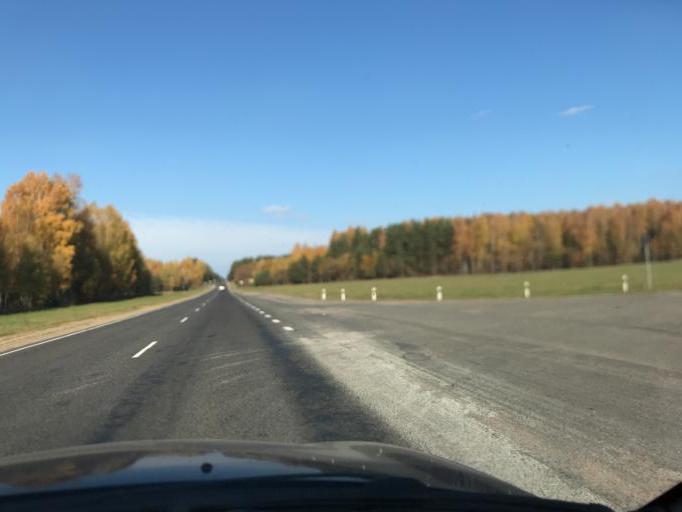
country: BY
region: Grodnenskaya
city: Lida
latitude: 53.9543
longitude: 25.2457
